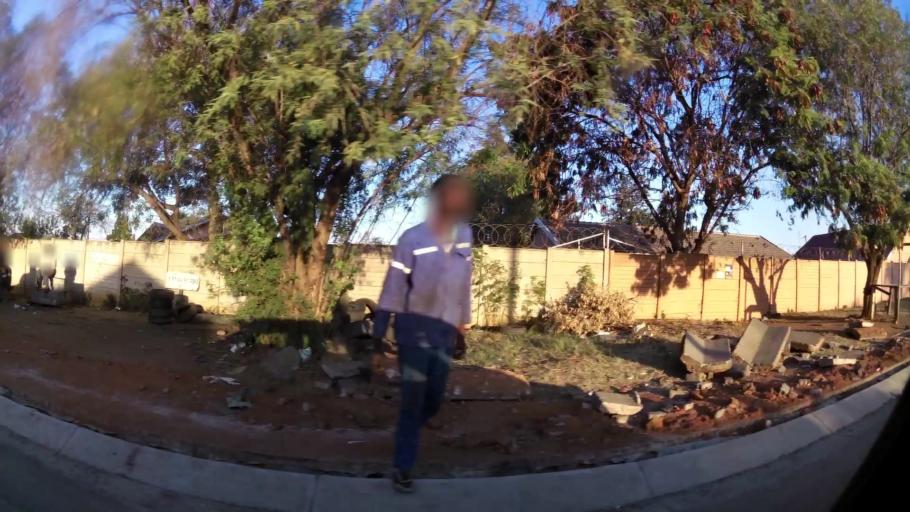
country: ZA
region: North-West
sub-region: Bojanala Platinum District Municipality
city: Rustenburg
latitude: -25.6391
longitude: 27.2097
